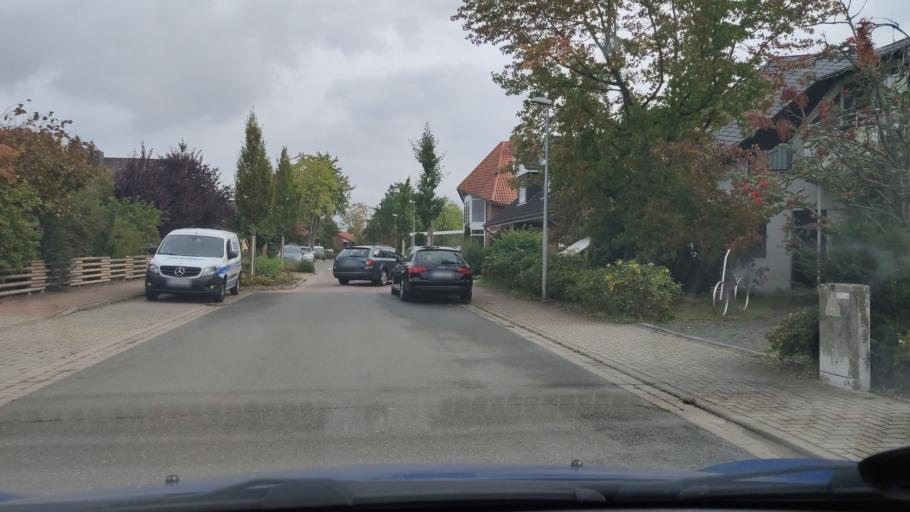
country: DE
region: Lower Saxony
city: Ronnenberg
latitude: 52.3655
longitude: 9.6493
